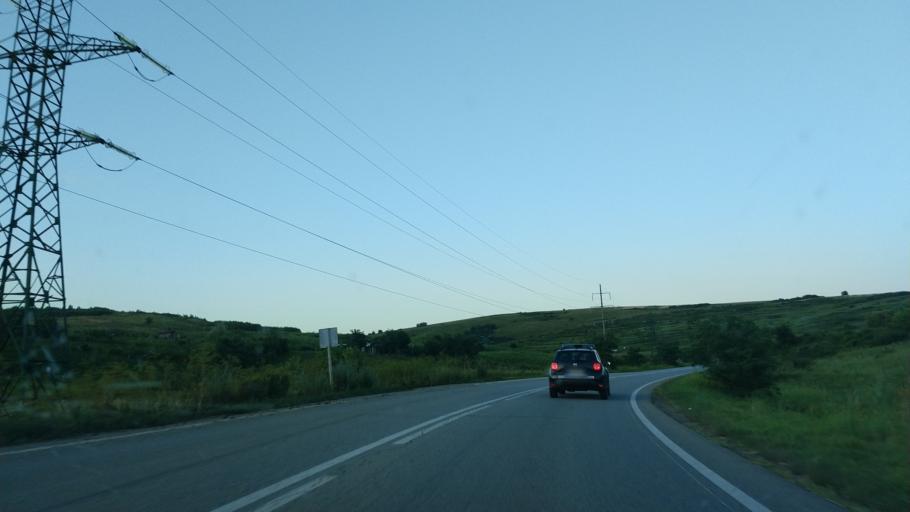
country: RO
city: Vanatori
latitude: 47.2634
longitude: 27.5386
